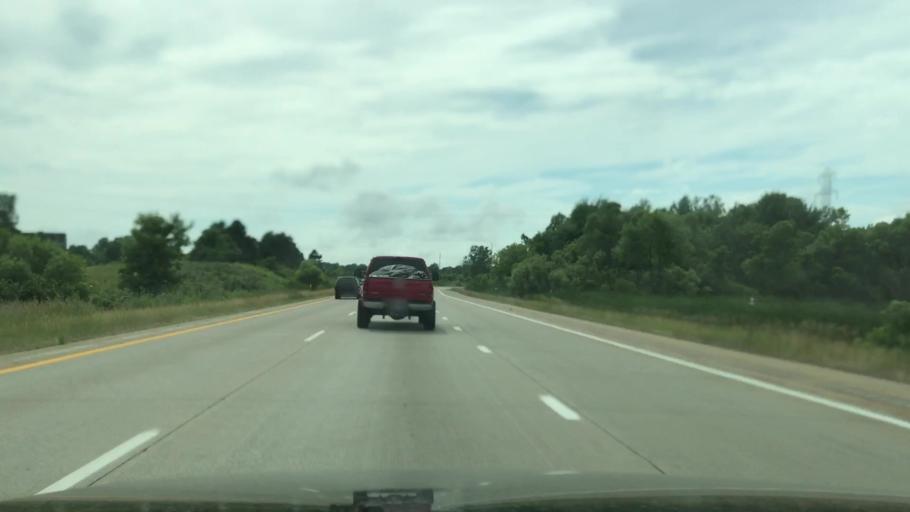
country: US
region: Michigan
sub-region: Kent County
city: Walker
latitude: 43.0182
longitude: -85.7557
